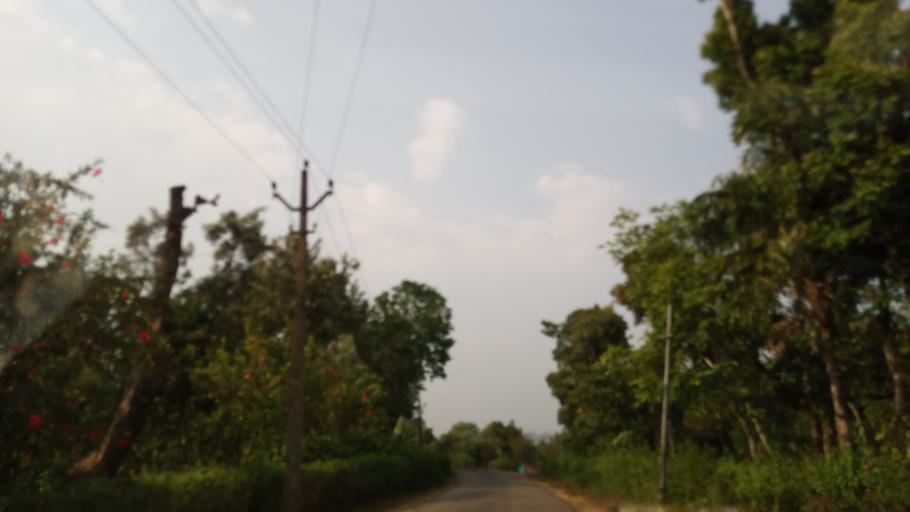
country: IN
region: Karnataka
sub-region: Chikmagalur
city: Mudigere
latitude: 13.0598
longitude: 75.6540
